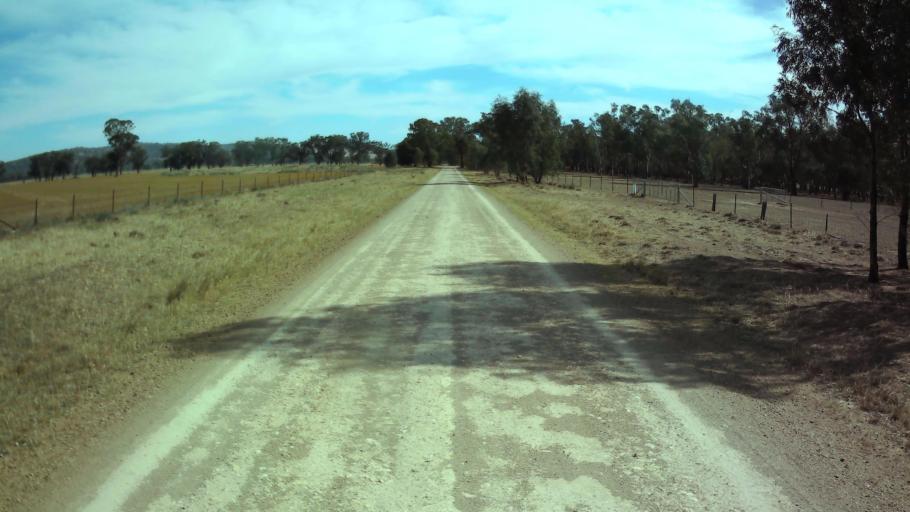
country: AU
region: New South Wales
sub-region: Weddin
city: Grenfell
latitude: -33.7048
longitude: 148.3015
